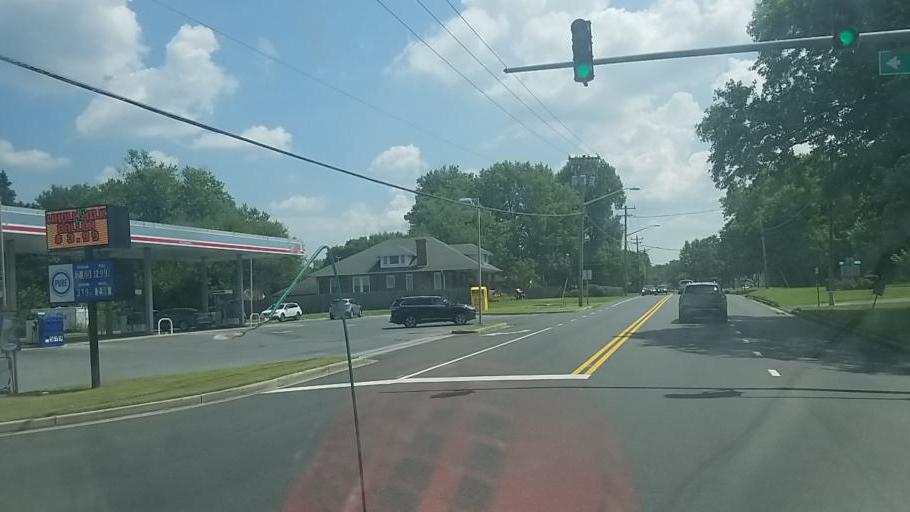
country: US
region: Maryland
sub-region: Wicomico County
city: Salisbury
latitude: 38.3734
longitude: -75.5546
